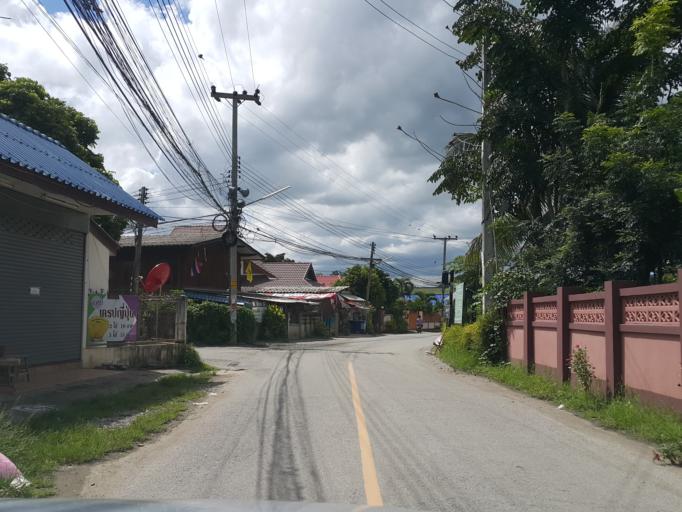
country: TH
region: Chiang Mai
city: San Kamphaeng
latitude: 18.7580
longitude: 99.1243
